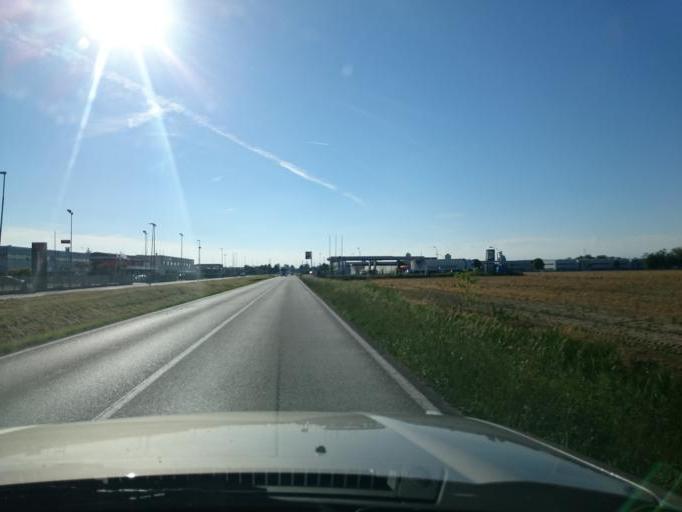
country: IT
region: Veneto
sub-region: Provincia di Venezia
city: Santa Maria di Sala
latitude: 45.5064
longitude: 12.0253
